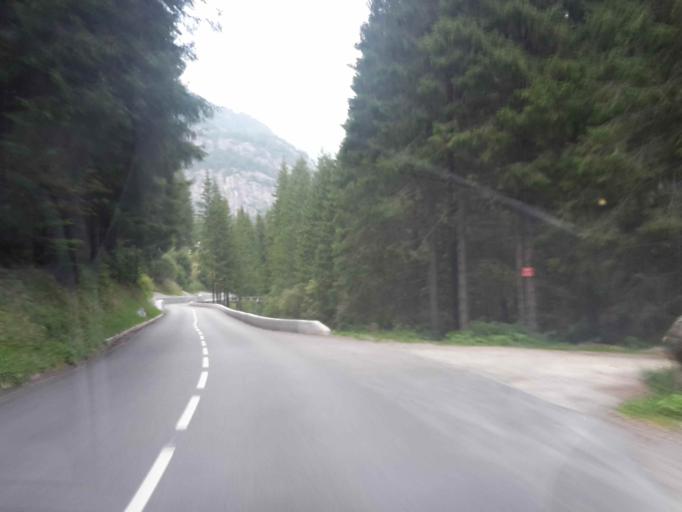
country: CH
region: Valais
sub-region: Saint-Maurice District
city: Salvan
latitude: 46.0368
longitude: 6.9365
